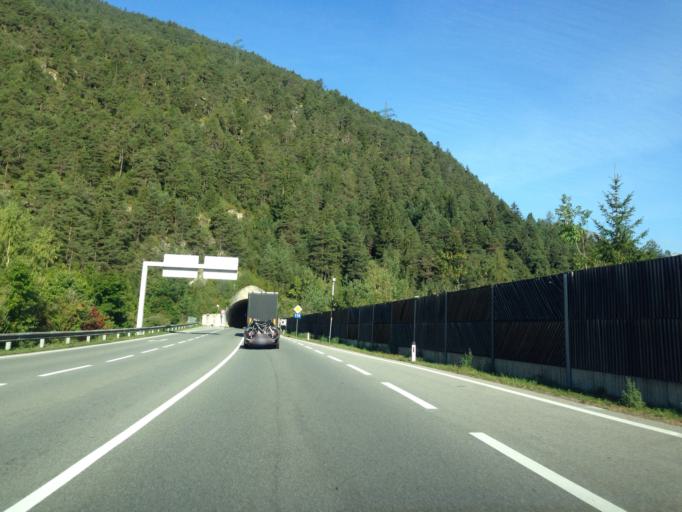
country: AT
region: Tyrol
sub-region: Politischer Bezirk Imst
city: Nassereith
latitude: 47.3057
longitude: 10.8400
